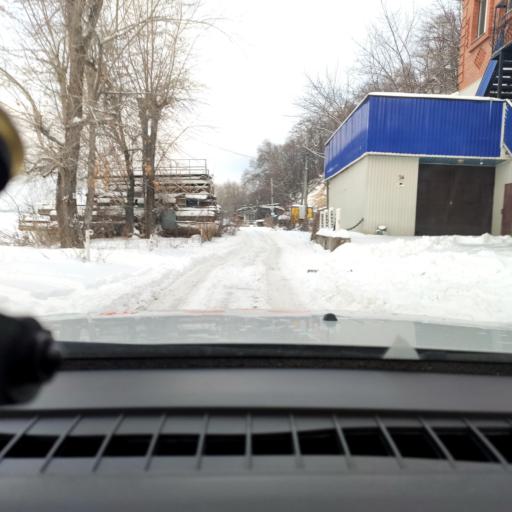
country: RU
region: Samara
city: Samara
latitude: 53.2860
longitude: 50.1906
